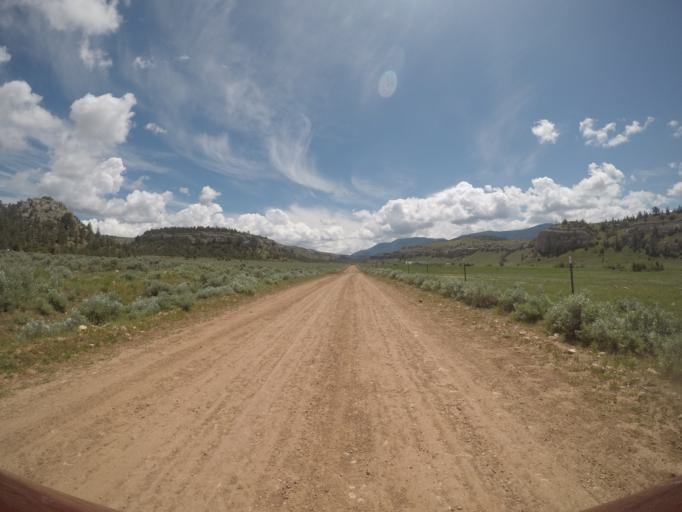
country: US
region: Montana
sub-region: Yellowstone County
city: Laurel
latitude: 45.2409
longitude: -108.6370
